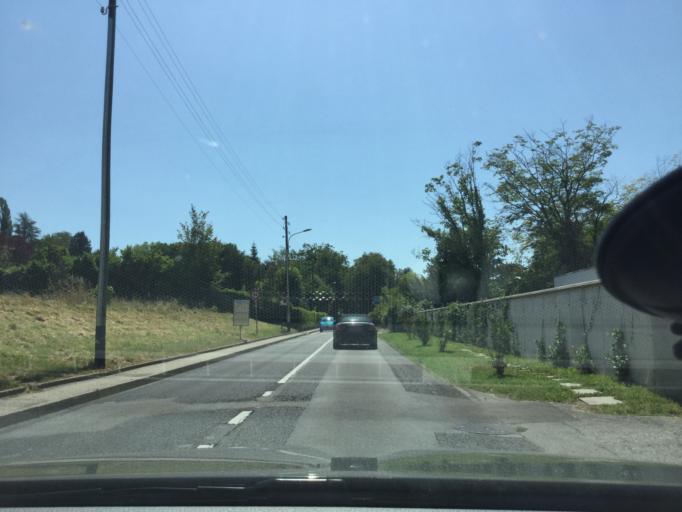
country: CH
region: Geneva
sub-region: Geneva
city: Corsier
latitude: 46.2688
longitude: 6.2177
